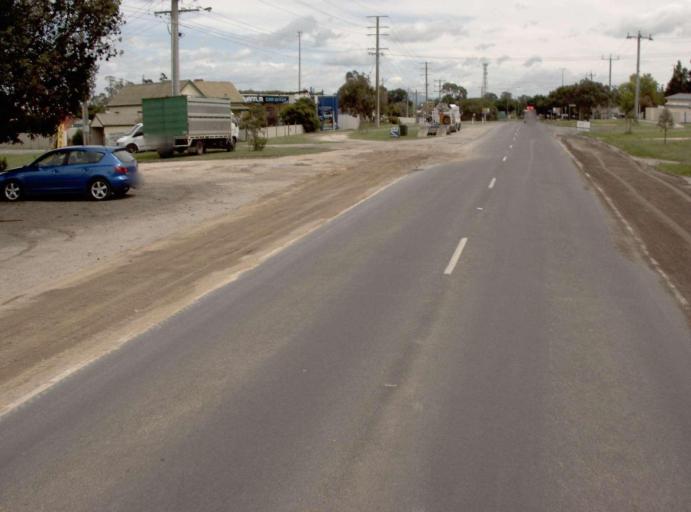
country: AU
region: Victoria
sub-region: Wellington
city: Sale
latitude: -37.9738
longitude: 146.9854
